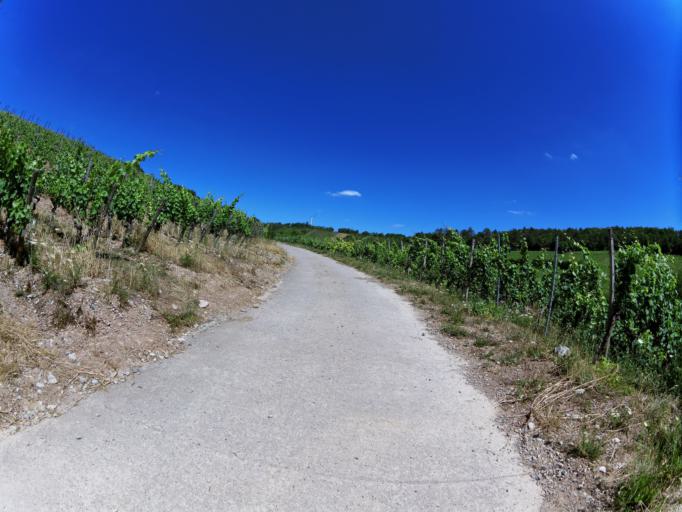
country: DE
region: Bavaria
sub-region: Regierungsbezirk Unterfranken
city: Thungersheim
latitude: 49.8873
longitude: 9.8580
